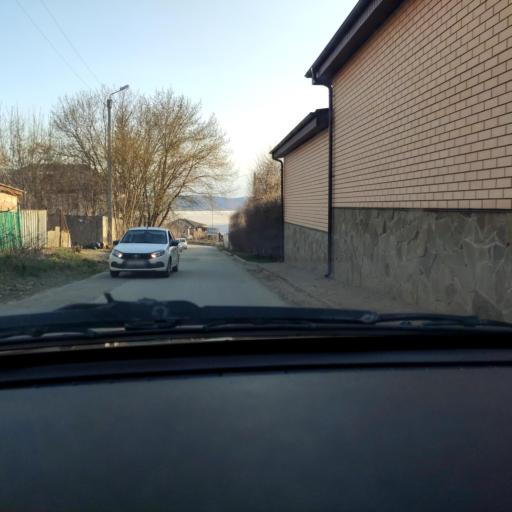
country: RU
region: Samara
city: Tol'yatti
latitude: 53.4762
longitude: 49.3682
